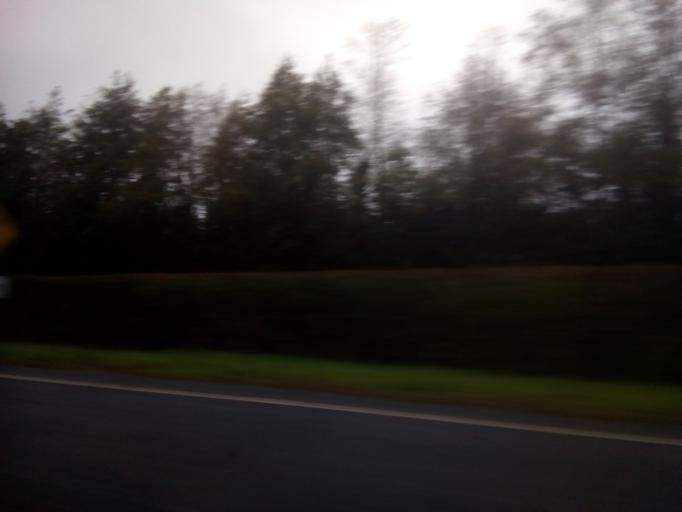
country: IE
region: Leinster
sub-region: An Iarmhi
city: An Muileann gCearr
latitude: 53.5460
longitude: -7.3251
